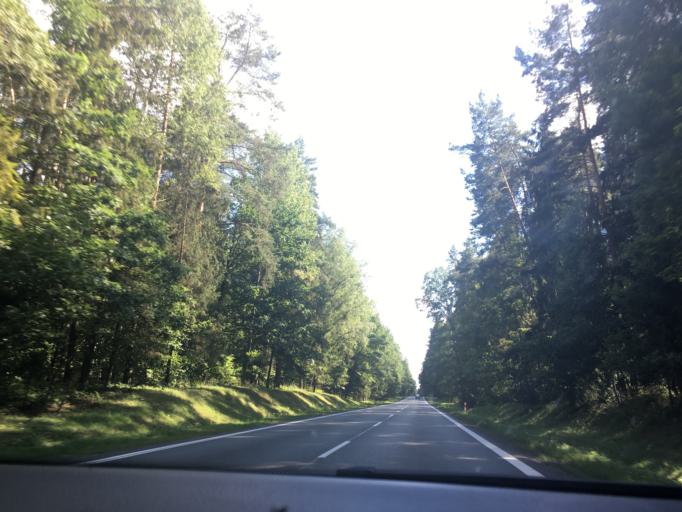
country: PL
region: Podlasie
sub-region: Powiat bialostocki
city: Wasilkow
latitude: 53.3063
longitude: 23.1258
